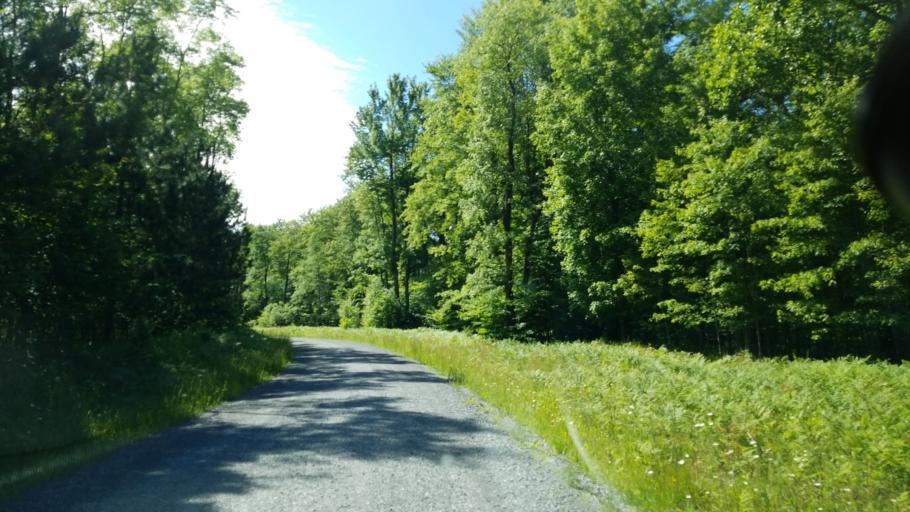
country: US
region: Pennsylvania
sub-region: Clearfield County
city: Clearfield
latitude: 41.1917
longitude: -78.4711
